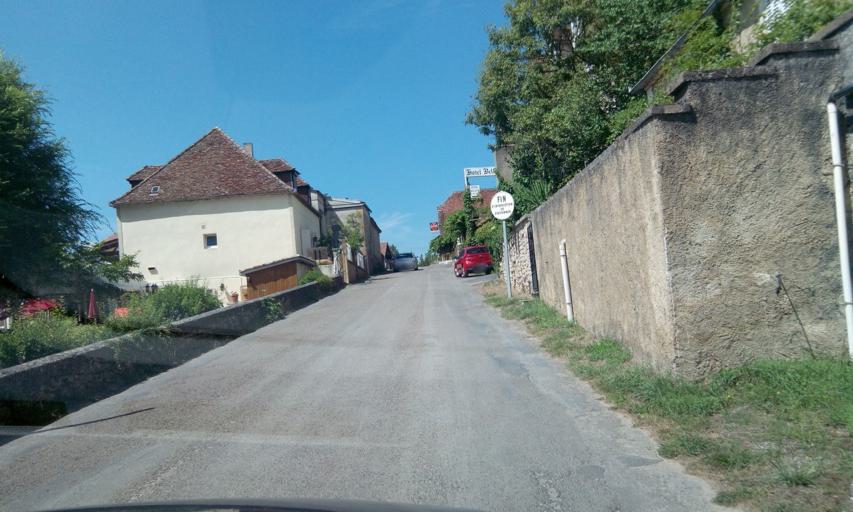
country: FR
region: Midi-Pyrenees
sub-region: Departement du Lot
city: Gramat
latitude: 44.8030
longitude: 1.6274
